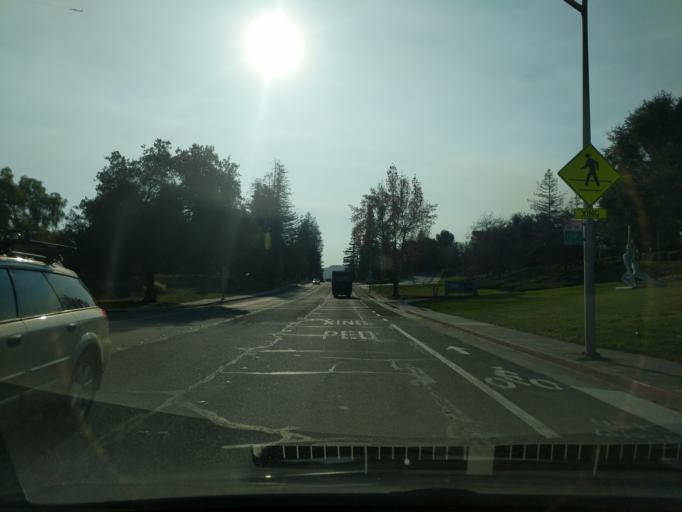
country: US
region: California
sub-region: Santa Clara County
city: Los Altos Hills
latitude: 37.4007
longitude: -122.1452
